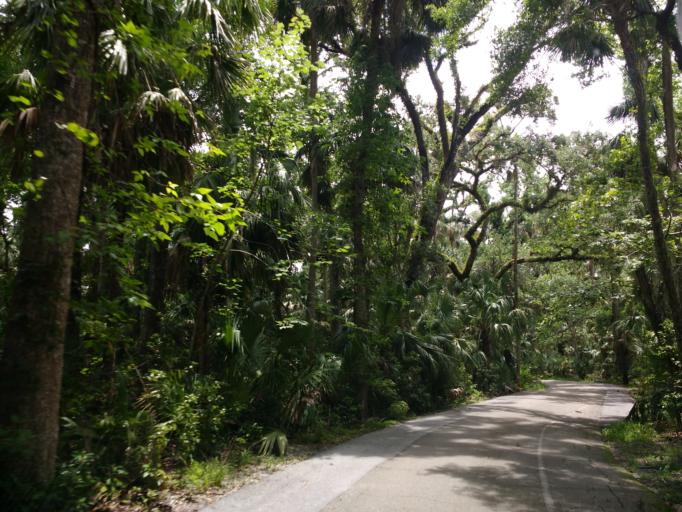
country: US
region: Florida
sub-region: Highlands County
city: Sebring
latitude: 27.4707
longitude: -81.5420
